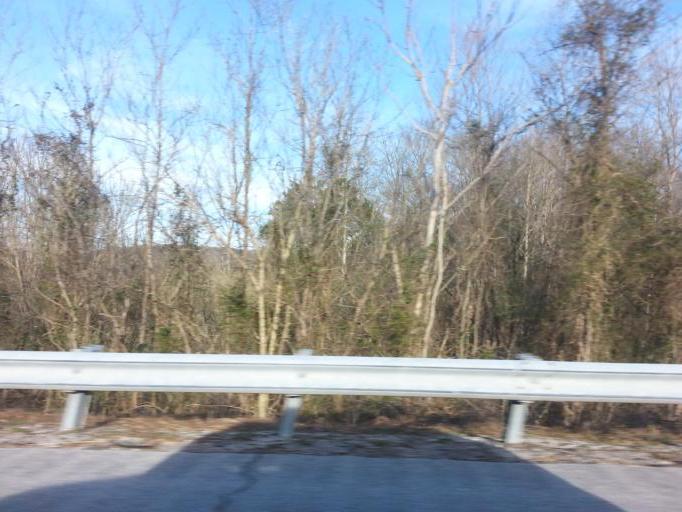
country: US
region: Tennessee
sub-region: White County
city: Sparta
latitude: 35.8958
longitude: -85.4730
